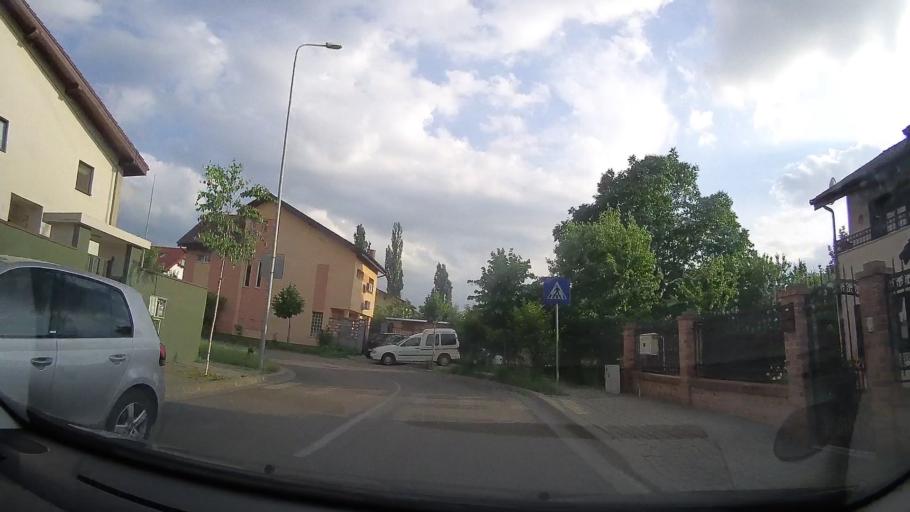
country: RO
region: Timis
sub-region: Comuna Dumbravita
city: Dumbravita
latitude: 45.7825
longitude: 21.2316
